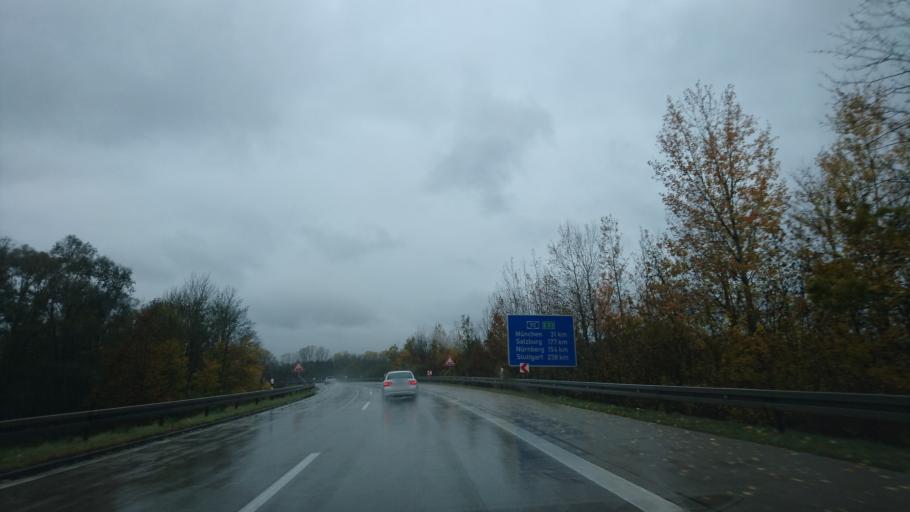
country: DE
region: Bavaria
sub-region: Upper Bavaria
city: Hallbergmoos
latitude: 48.3513
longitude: 11.7309
